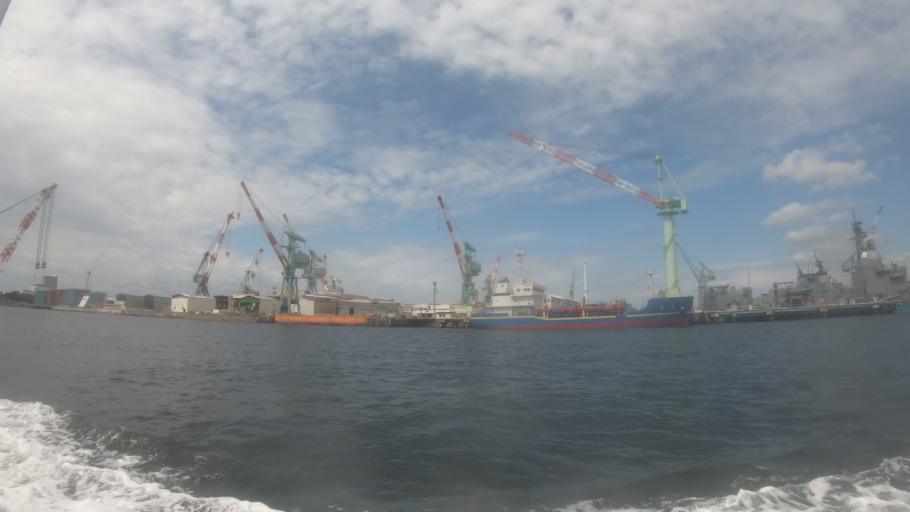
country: JP
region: Kanagawa
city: Yokohama
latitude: 35.3891
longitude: 139.6380
